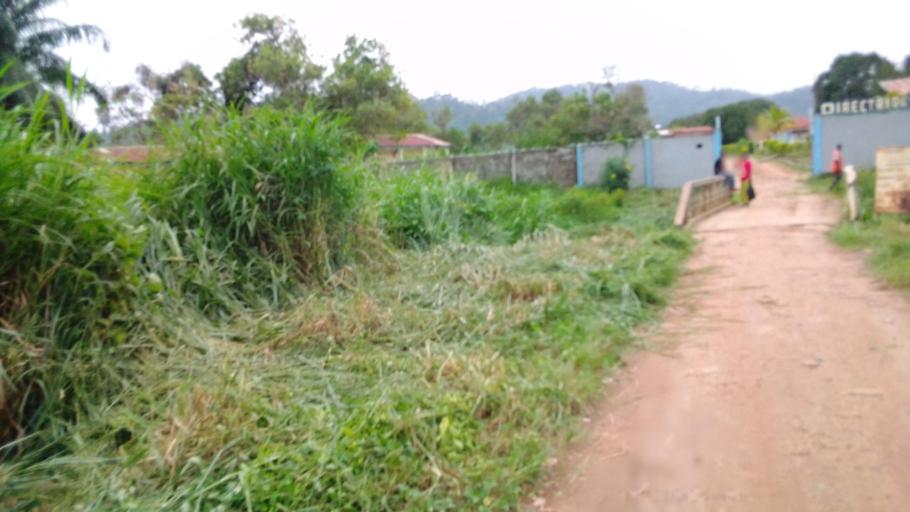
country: SL
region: Eastern Province
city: Kenema
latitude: 7.8609
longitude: -11.2018
